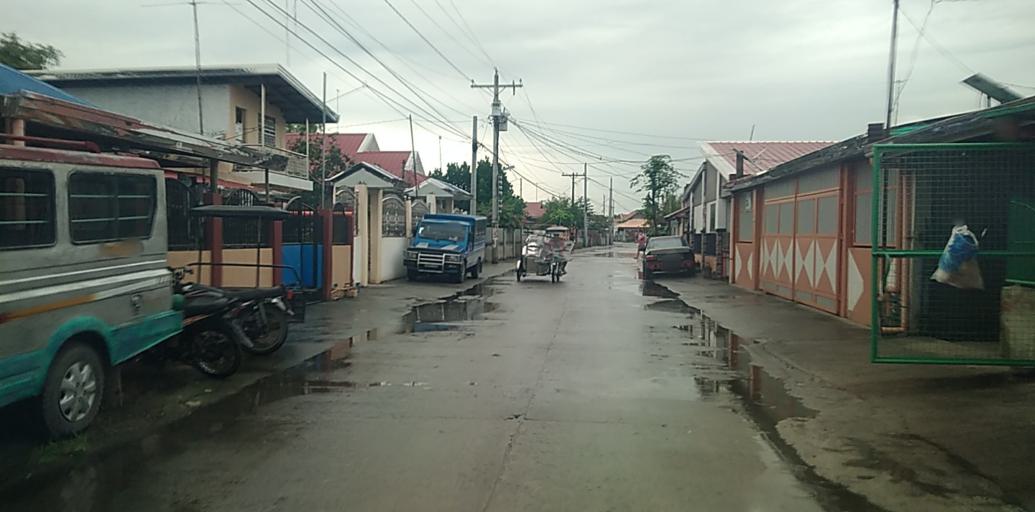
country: PH
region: Central Luzon
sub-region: Province of Pampanga
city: Arayat
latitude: 15.1395
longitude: 120.7367
